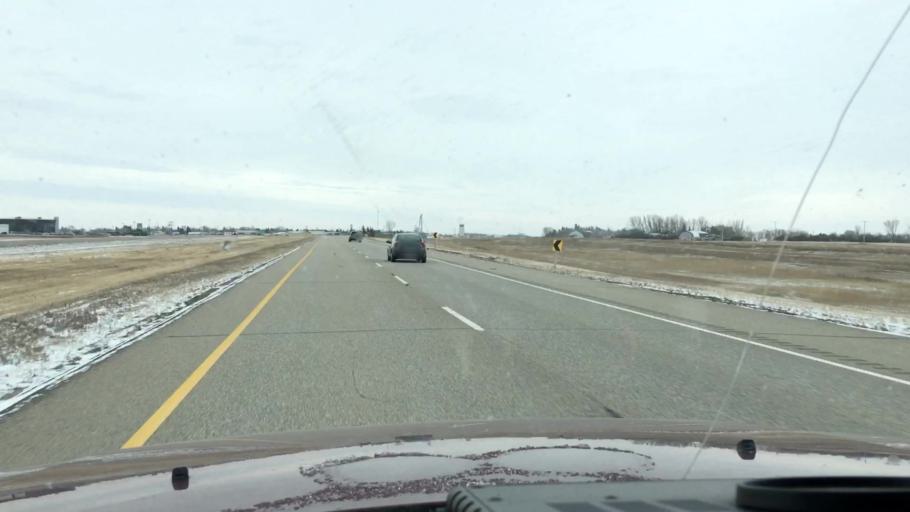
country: CA
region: Saskatchewan
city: Watrous
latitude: 51.2774
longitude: -106.0115
